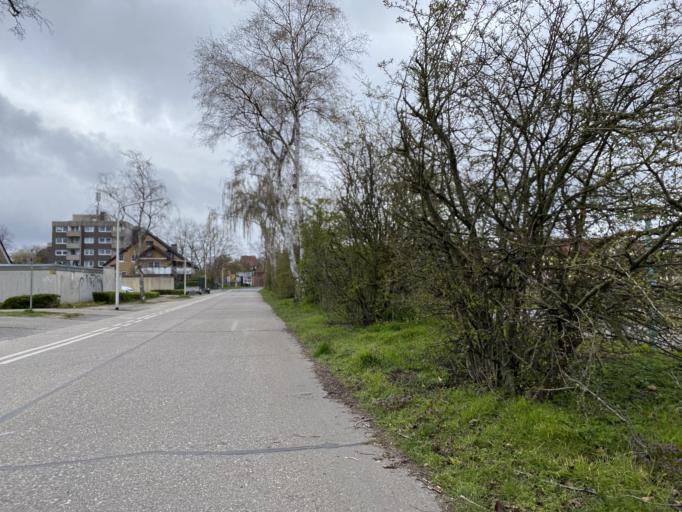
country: DE
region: North Rhine-Westphalia
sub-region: Regierungsbezirk Arnsberg
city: Hamm
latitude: 51.6875
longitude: 7.8834
